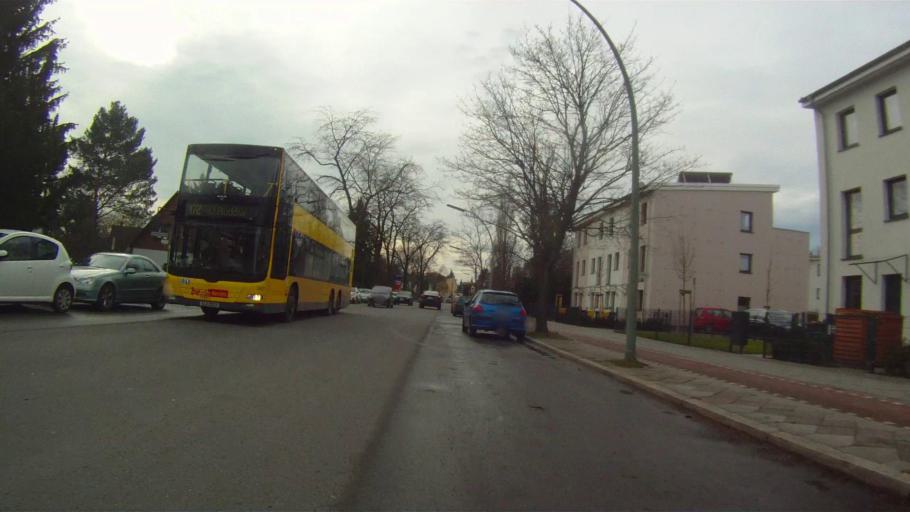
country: DE
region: Berlin
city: Lichtenrade
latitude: 52.4005
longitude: 13.4110
